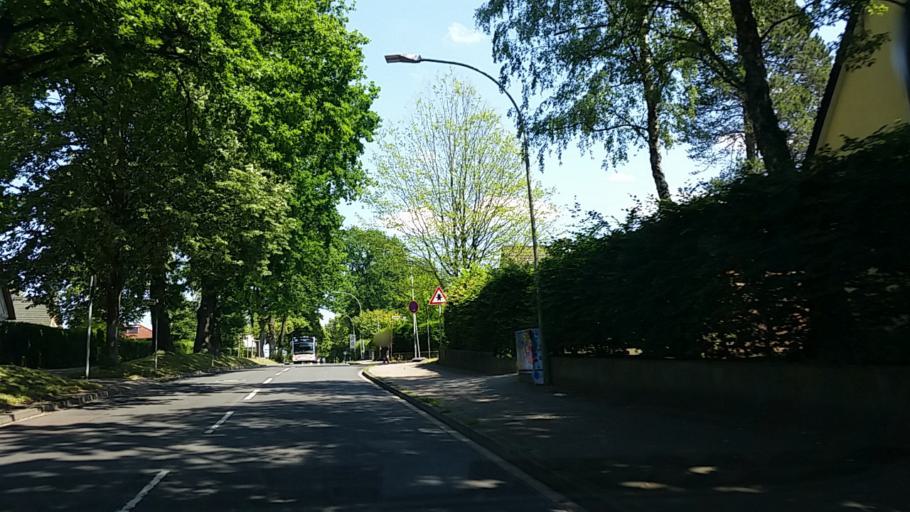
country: DE
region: Schleswig-Holstein
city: Glinde
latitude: 53.5407
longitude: 10.2171
